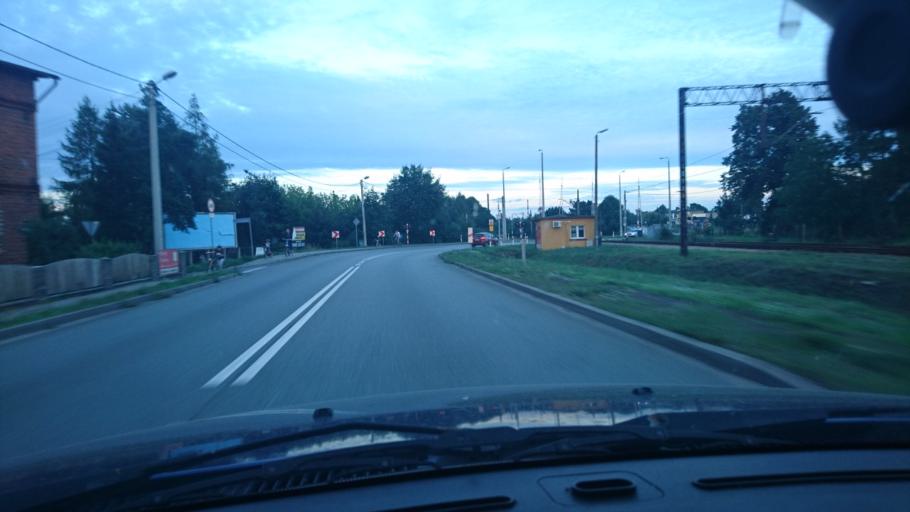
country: PL
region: Silesian Voivodeship
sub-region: Powiat tarnogorski
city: Tarnowskie Gory
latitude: 50.4719
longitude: 18.8040
